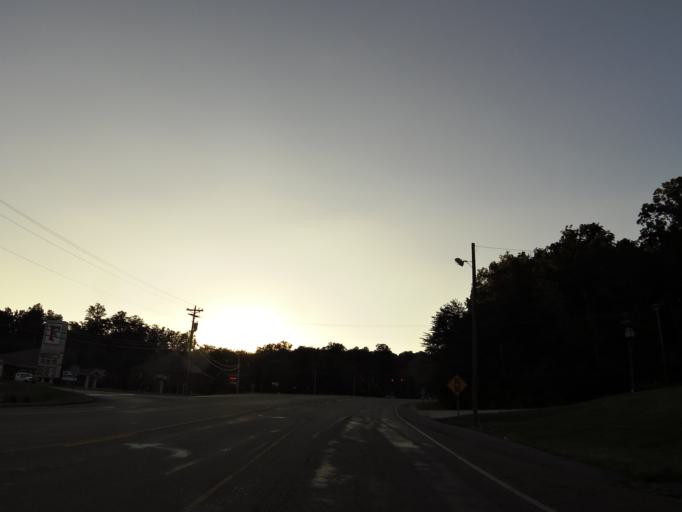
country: US
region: Tennessee
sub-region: Jefferson County
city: Dandridge
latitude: 36.0178
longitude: -83.4238
